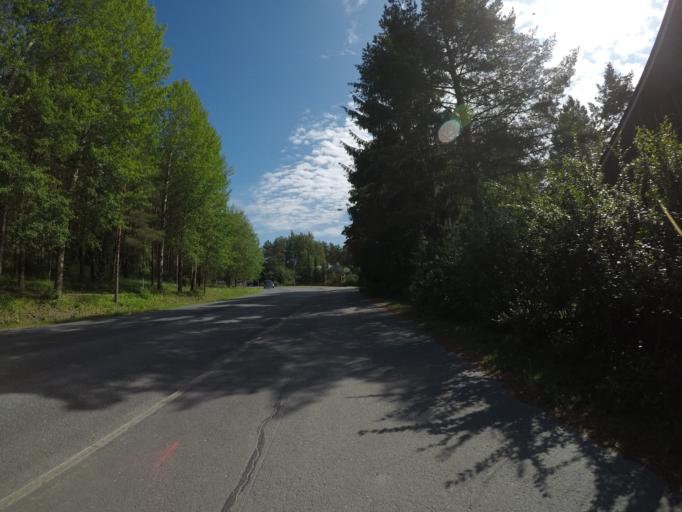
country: FI
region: Haeme
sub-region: Haemeenlinna
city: Haemeenlinna
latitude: 60.9865
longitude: 24.4086
